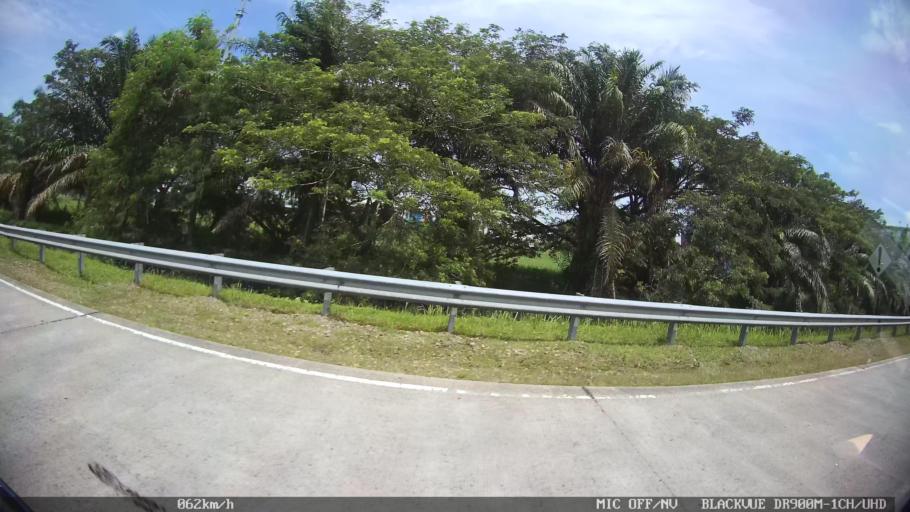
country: ID
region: North Sumatra
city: Percut
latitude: 3.6289
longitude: 98.8722
